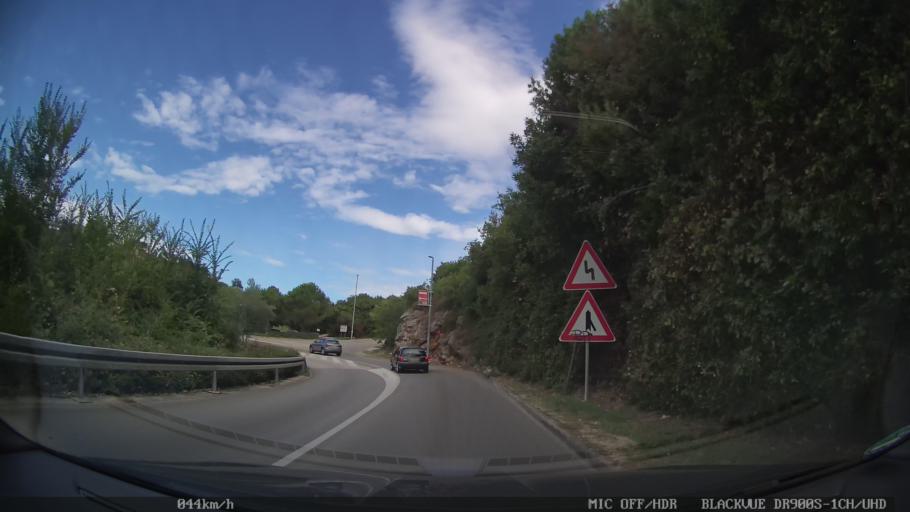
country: HR
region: Primorsko-Goranska
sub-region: Grad Krk
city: Krk
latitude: 45.0306
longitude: 14.5752
